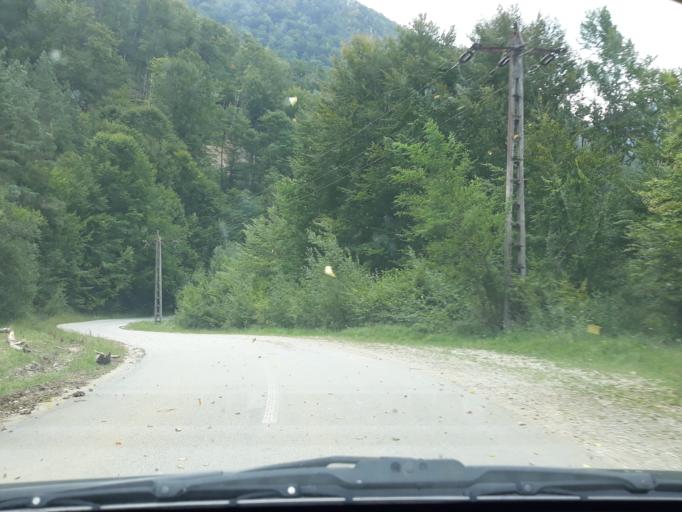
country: RO
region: Bihor
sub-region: Comuna Pietroasa
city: Pietroasa
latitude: 46.5995
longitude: 22.6374
